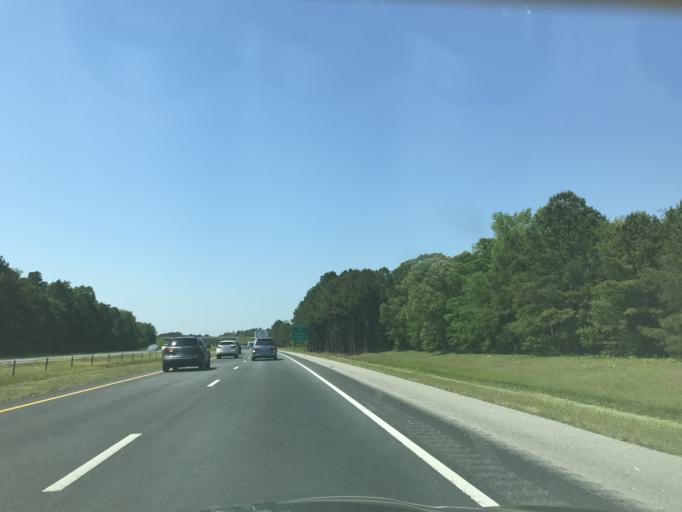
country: US
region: North Carolina
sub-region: Johnston County
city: Benson
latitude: 35.3641
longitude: -78.4900
